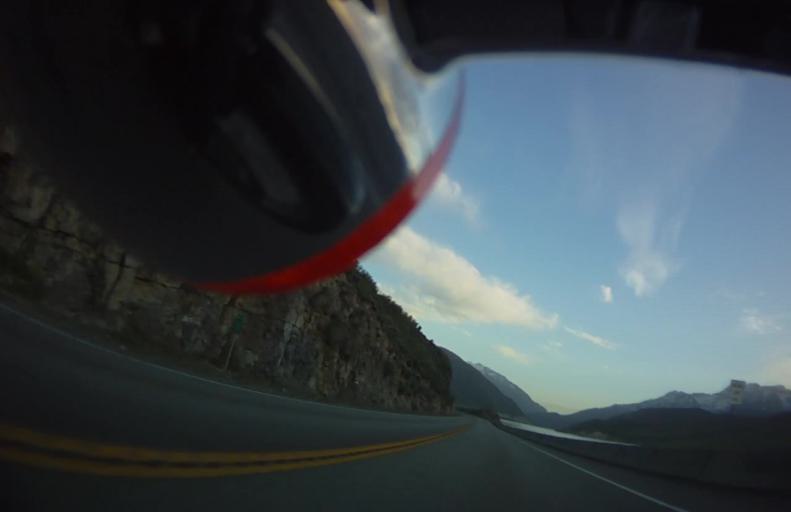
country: US
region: Utah
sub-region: Wasatch County
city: Midway
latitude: 40.4387
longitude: -111.4916
